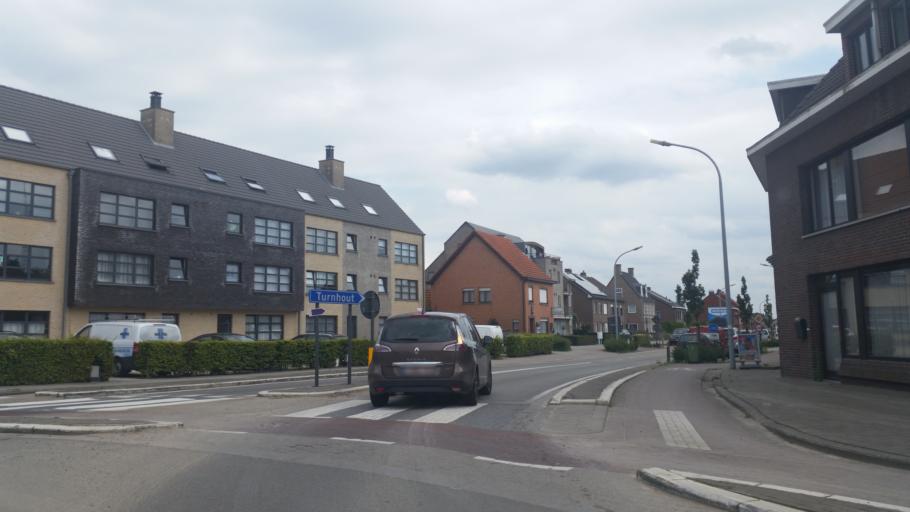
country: BE
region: Flanders
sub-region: Provincie Antwerpen
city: Merksplas
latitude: 51.3540
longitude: 4.8644
